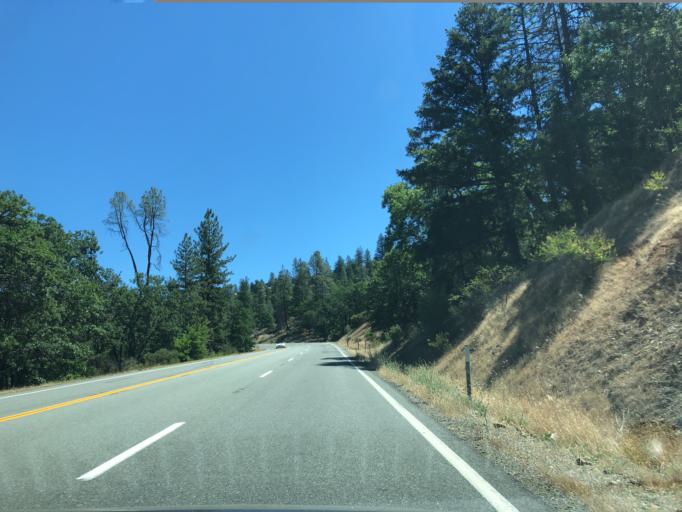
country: US
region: California
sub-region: Trinity County
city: Weaverville
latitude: 40.6681
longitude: -122.8868
